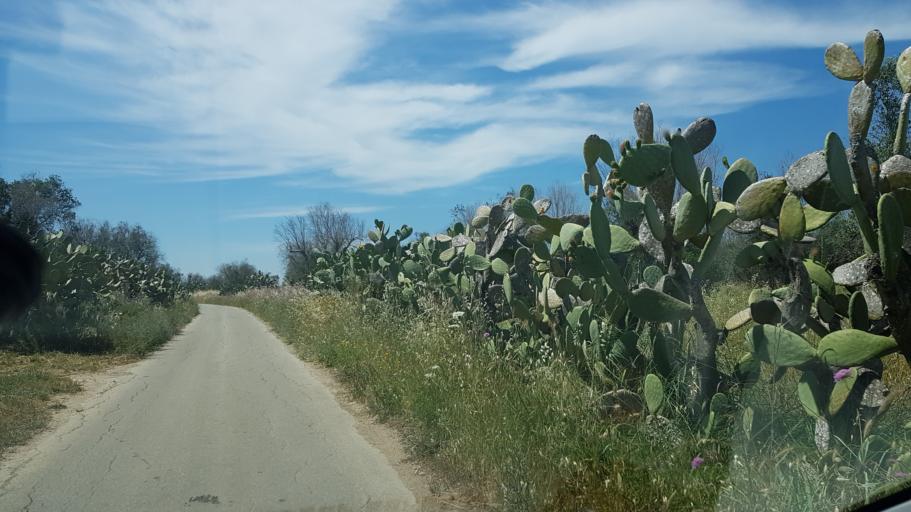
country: IT
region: Apulia
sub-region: Provincia di Brindisi
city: San Pietro Vernotico
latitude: 40.5285
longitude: 18.0039
